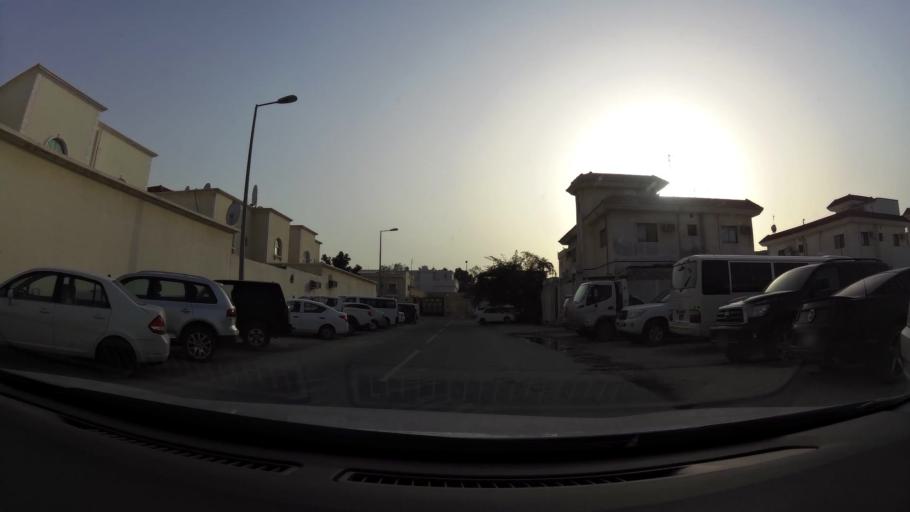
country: QA
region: Baladiyat ar Rayyan
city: Ar Rayyan
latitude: 25.2369
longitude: 51.4486
